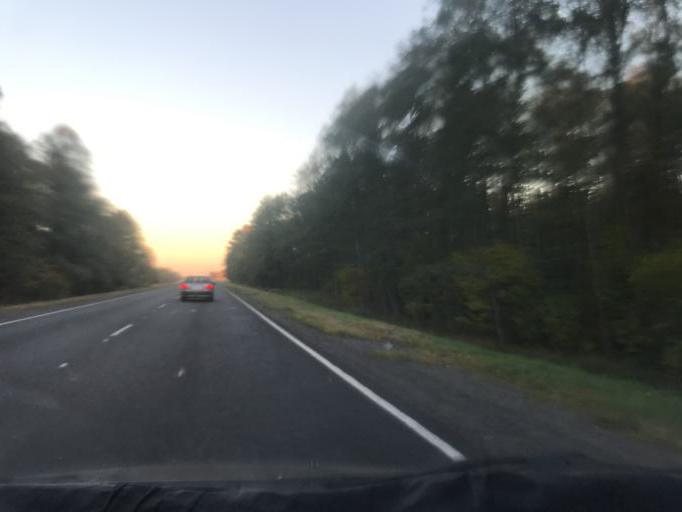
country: BY
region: Gomel
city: Kalinkavichy
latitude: 52.1703
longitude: 29.2059
